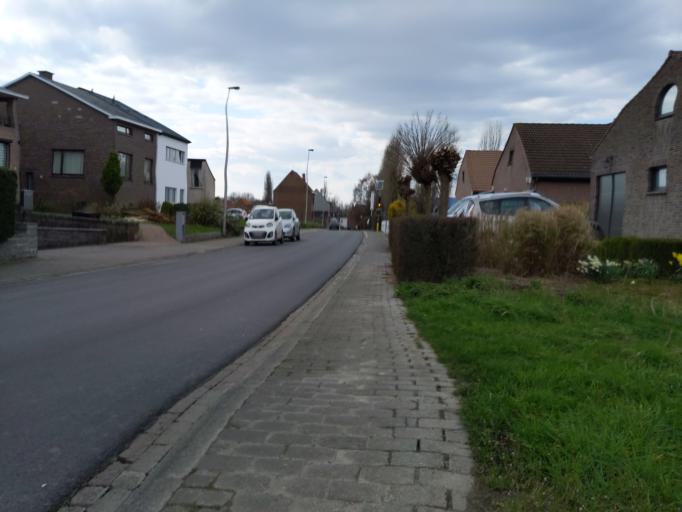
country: BE
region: Flanders
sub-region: Provincie Vlaams-Brabant
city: Ternat
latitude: 50.8680
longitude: 4.1826
